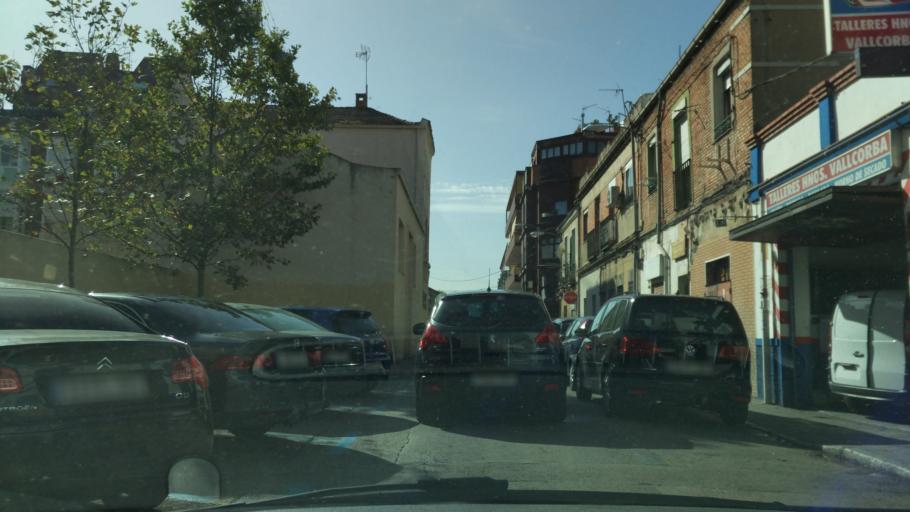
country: ES
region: Madrid
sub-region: Provincia de Madrid
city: Tetuan de las Victorias
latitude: 40.4641
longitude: -3.6991
